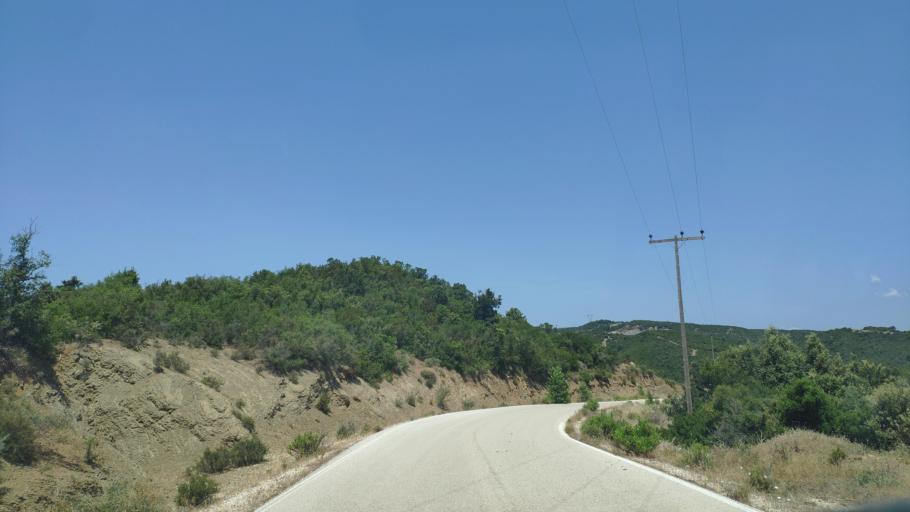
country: GR
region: West Greece
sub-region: Nomos Aitolias kai Akarnanias
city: Sardinia
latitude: 38.8719
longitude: 21.2812
